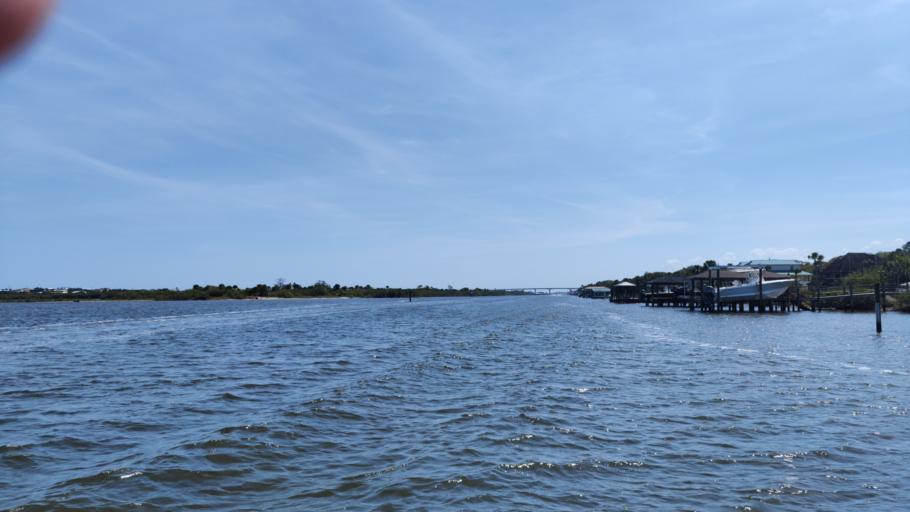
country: US
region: Florida
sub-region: Flagler County
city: Flagler Beach
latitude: 29.4970
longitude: -81.1433
